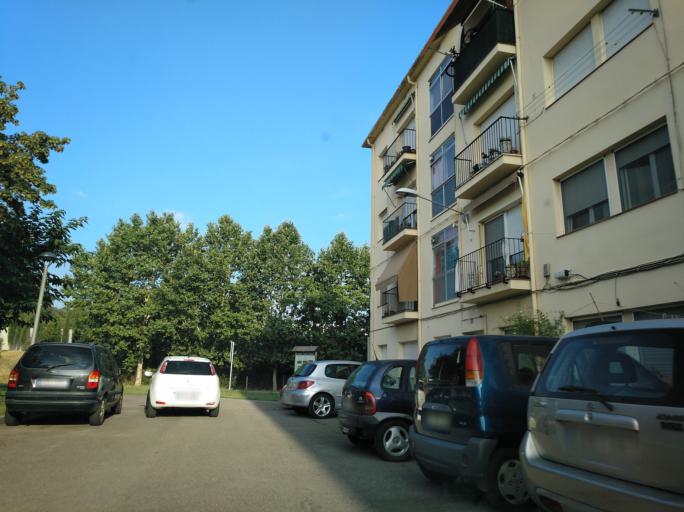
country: ES
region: Catalonia
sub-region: Provincia de Girona
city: Salt
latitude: 41.9743
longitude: 2.7793
